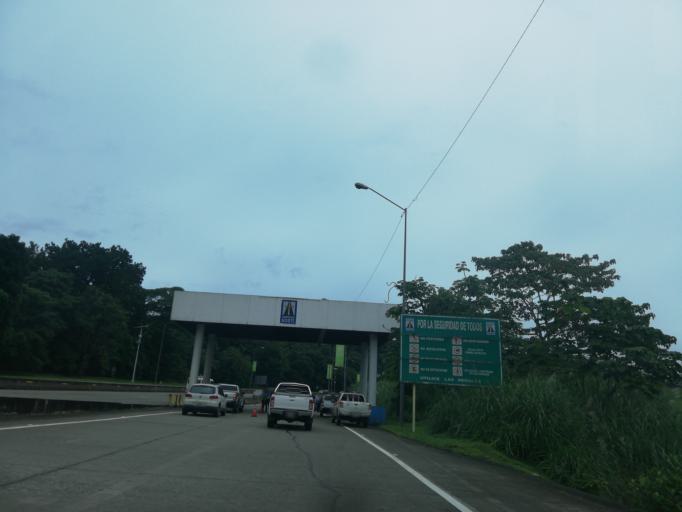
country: PA
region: Panama
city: Panama
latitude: 9.0118
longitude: -79.5429
